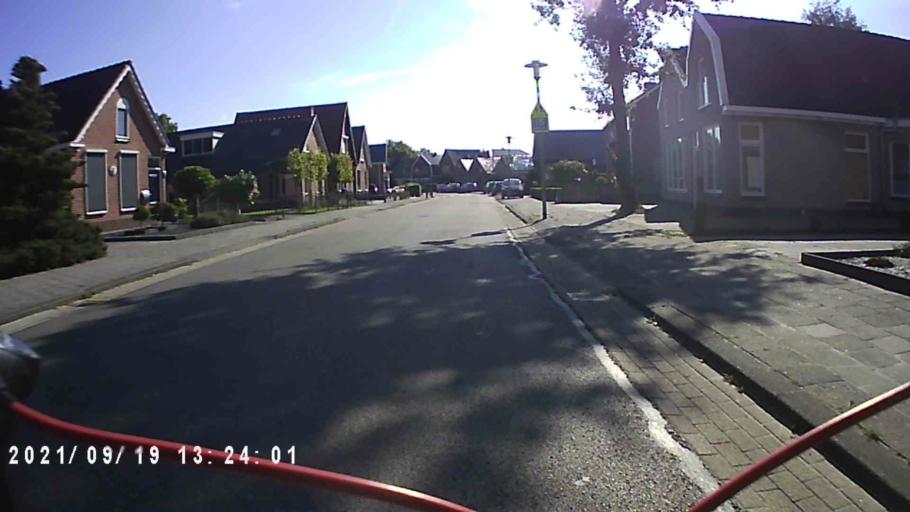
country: NL
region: Groningen
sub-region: Gemeente  Oldambt
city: Winschoten
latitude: 53.1560
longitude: 7.0057
